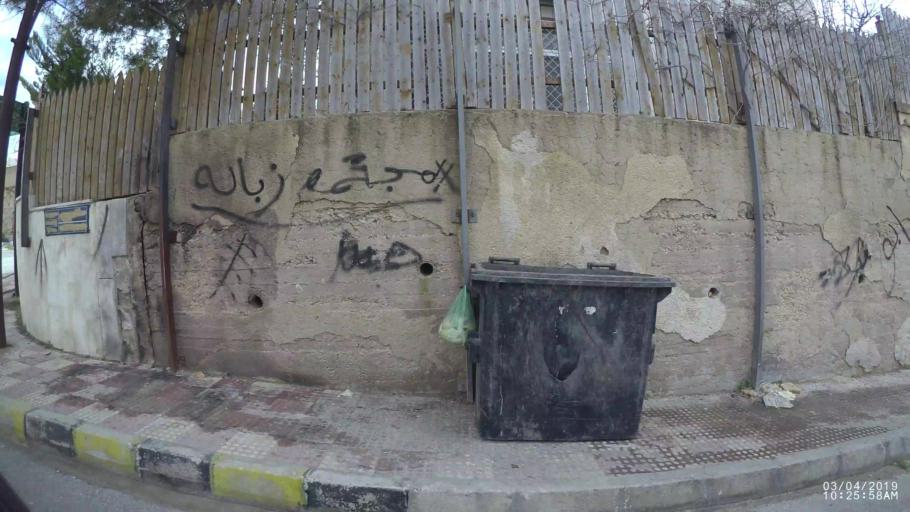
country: JO
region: Amman
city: Wadi as Sir
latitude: 31.9492
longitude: 35.8247
